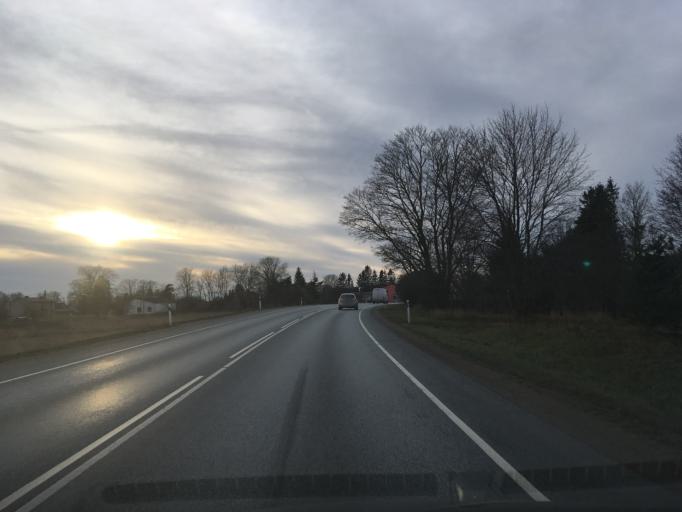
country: EE
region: Ida-Virumaa
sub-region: Puessi linn
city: Pussi
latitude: 59.4048
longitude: 27.0992
